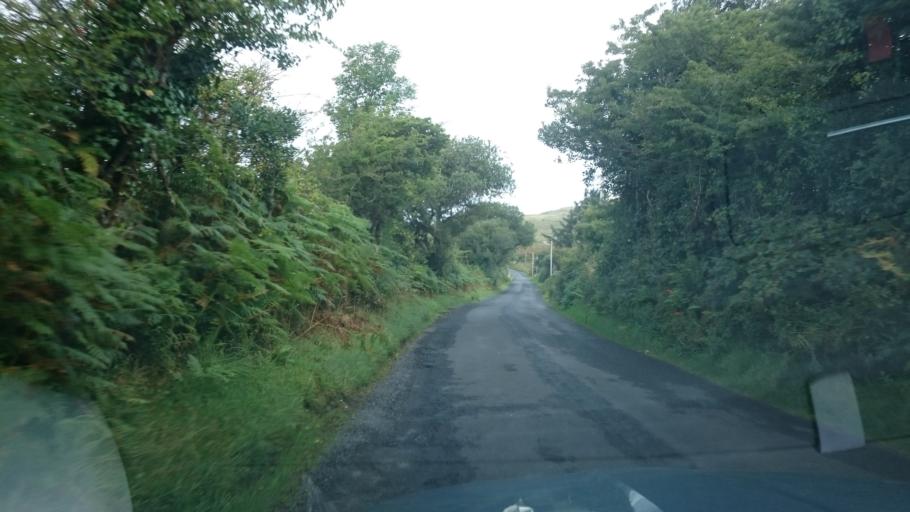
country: IE
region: Connaught
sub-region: Maigh Eo
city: Westport
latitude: 53.9141
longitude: -9.5535
